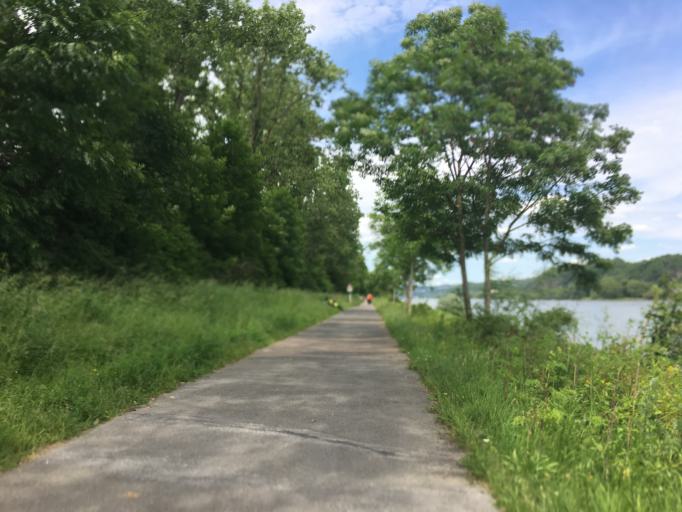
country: DE
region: Rheinland-Pfalz
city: Bad Breisig
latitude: 50.5223
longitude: 7.2929
